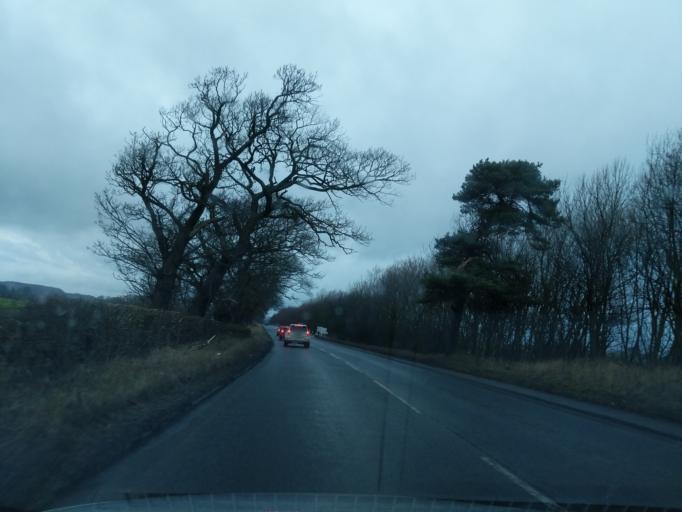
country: GB
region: Scotland
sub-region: Edinburgh
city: Newbridge
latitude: 55.9181
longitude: -3.4094
